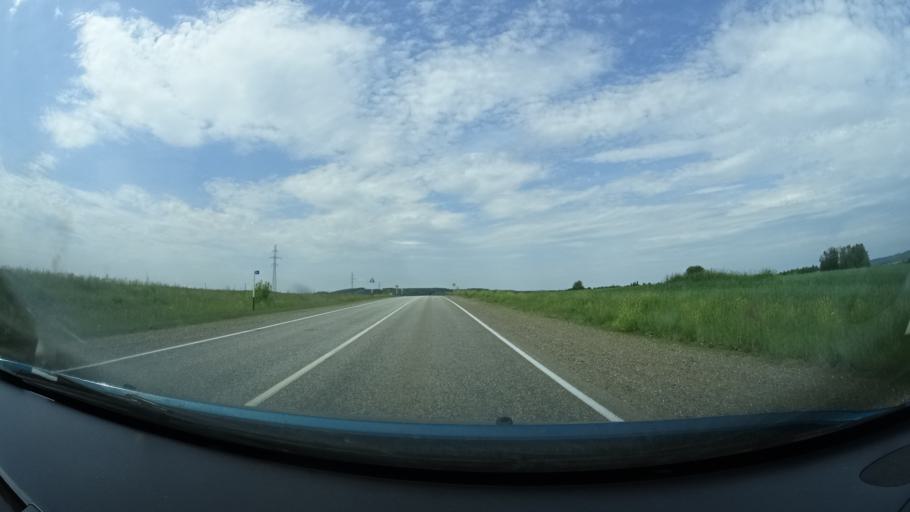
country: RU
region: Perm
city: Barda
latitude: 57.0945
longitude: 55.5341
